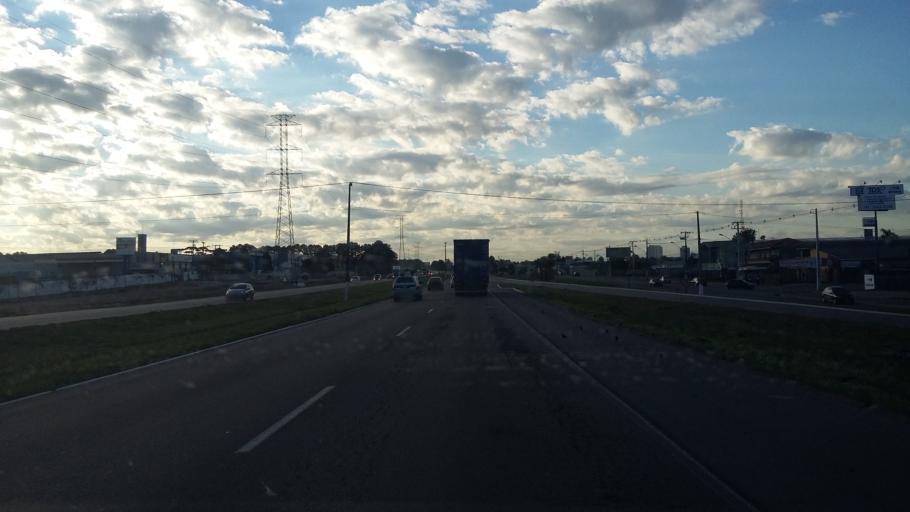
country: BR
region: Parana
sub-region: Curitiba
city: Curitiba
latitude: -25.4813
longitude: -49.3489
